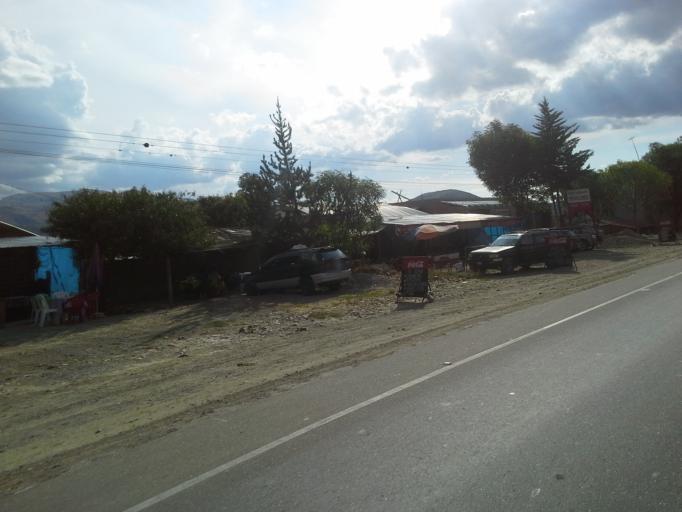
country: BO
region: Cochabamba
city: Tarata
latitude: -17.5363
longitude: -66.0777
